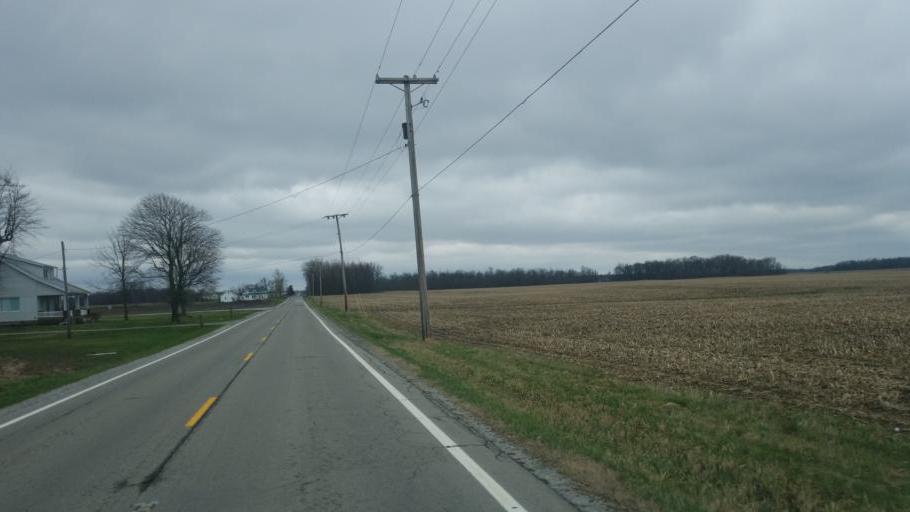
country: US
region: Ohio
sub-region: Hardin County
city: Kenton
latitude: 40.7010
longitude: -83.5754
